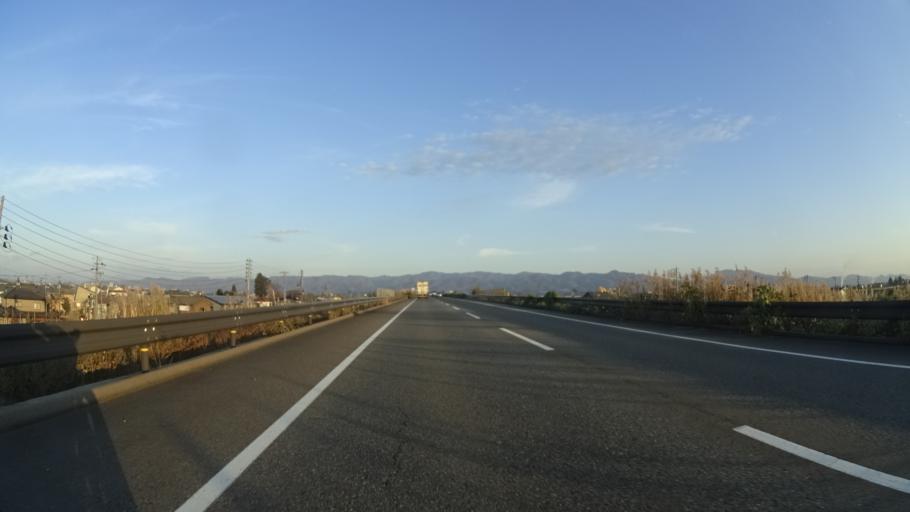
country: JP
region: Niigata
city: Nagaoka
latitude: 37.4339
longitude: 138.8102
